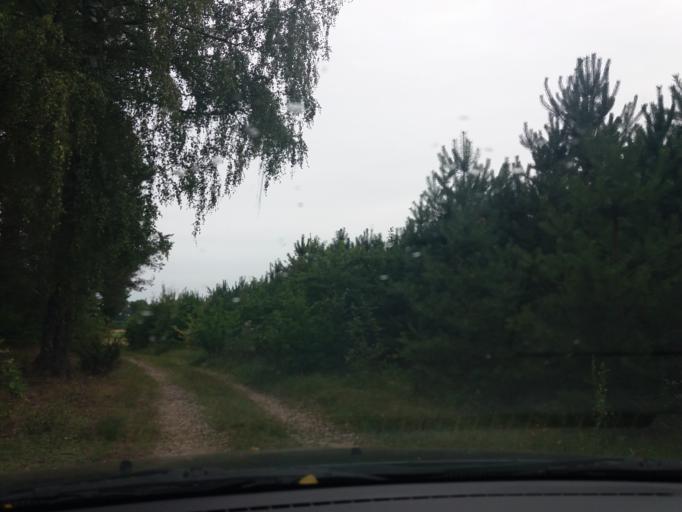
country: PL
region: Masovian Voivodeship
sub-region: Powiat mlawski
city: Wieczfnia Koscielna
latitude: 53.2334
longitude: 20.4831
